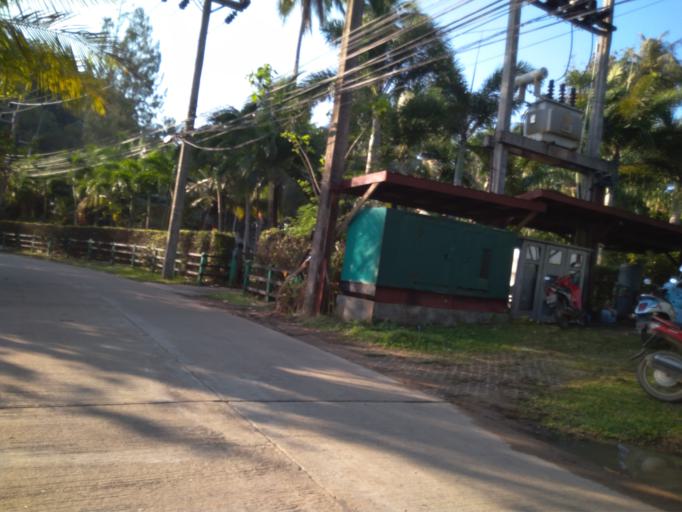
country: TH
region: Phangnga
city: Ko Yao
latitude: 8.1044
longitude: 98.6227
